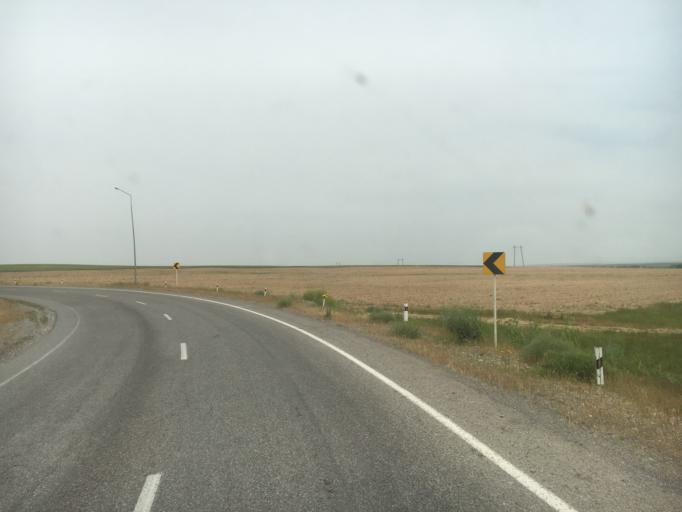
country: KZ
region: Ongtustik Qazaqstan
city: Temirlanovka
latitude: 42.5297
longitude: 69.3462
